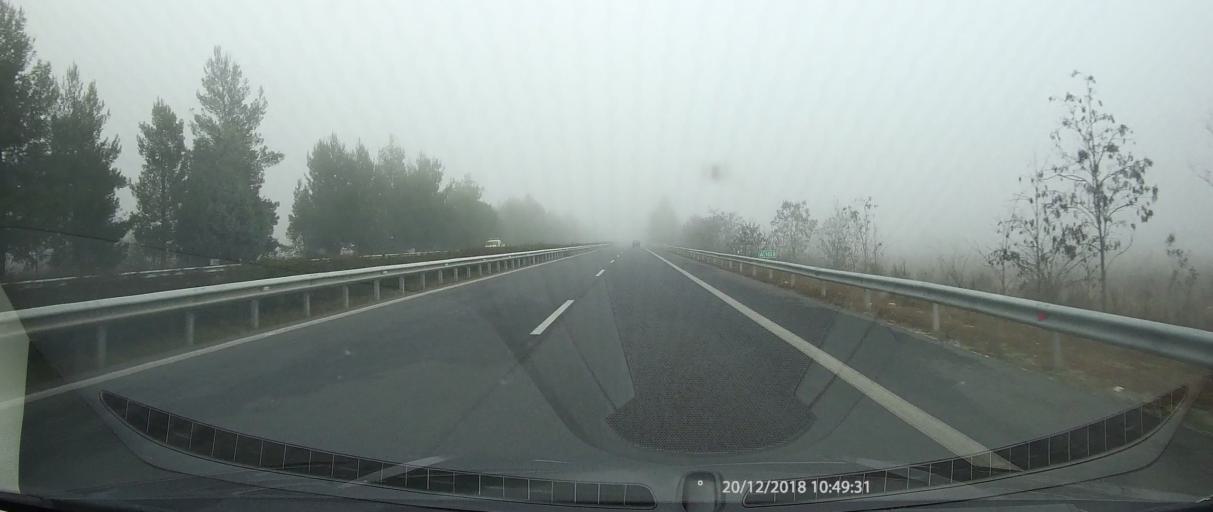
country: GR
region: Peloponnese
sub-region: Nomos Arkadias
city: Tripoli
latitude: 37.5417
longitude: 22.4161
